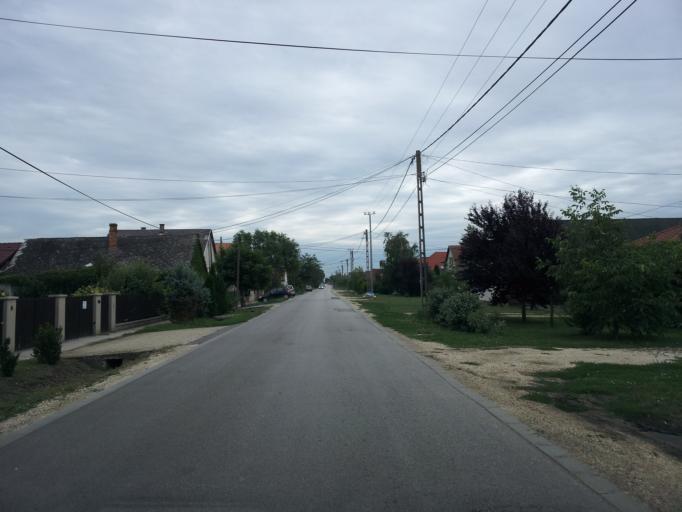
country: HU
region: Pest
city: Tarnok
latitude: 47.3736
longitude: 18.8418
